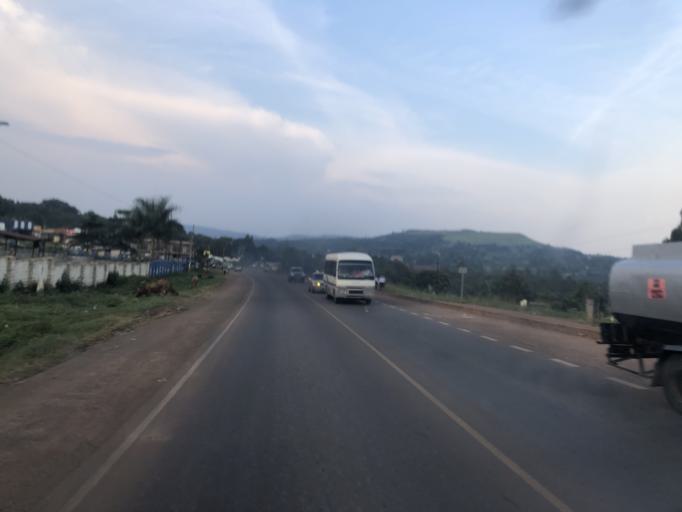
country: UG
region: Central Region
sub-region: Mpigi District
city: Mpigi
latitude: 0.2197
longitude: 32.3339
